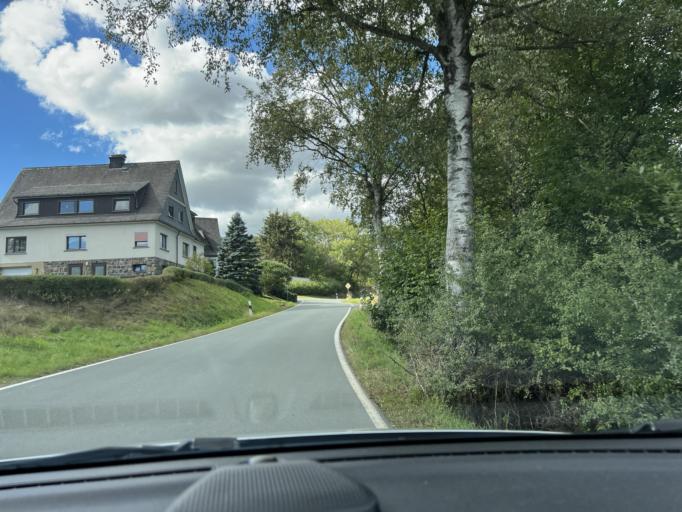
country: DE
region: North Rhine-Westphalia
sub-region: Regierungsbezirk Arnsberg
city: Bad Berleburg
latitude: 51.0026
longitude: 8.4390
